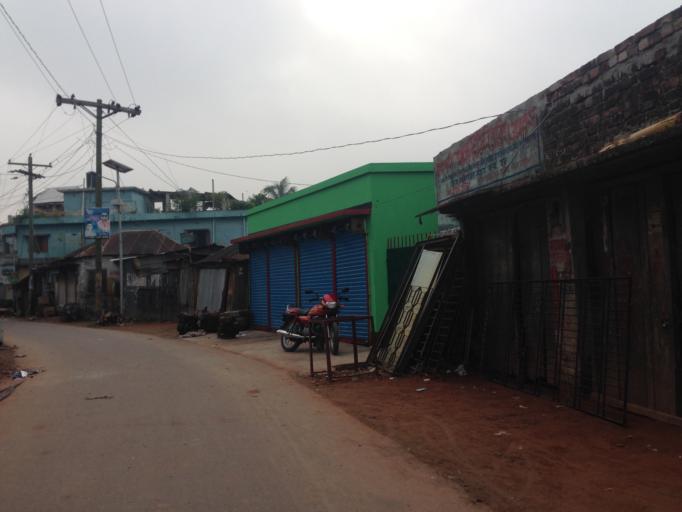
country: BD
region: Khulna
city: Kalia
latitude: 23.0410
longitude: 89.6313
